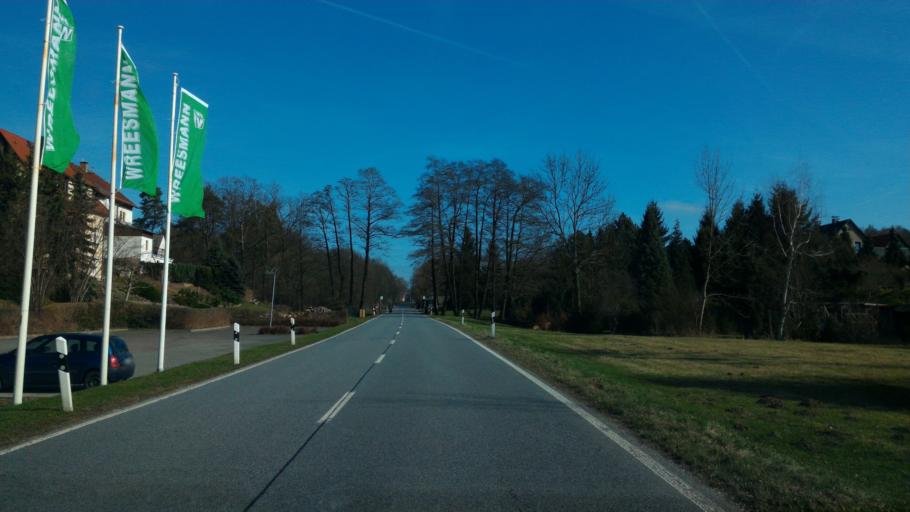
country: DE
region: Saxony
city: Durrrohrsdorf
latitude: 51.0253
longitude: 14.0072
